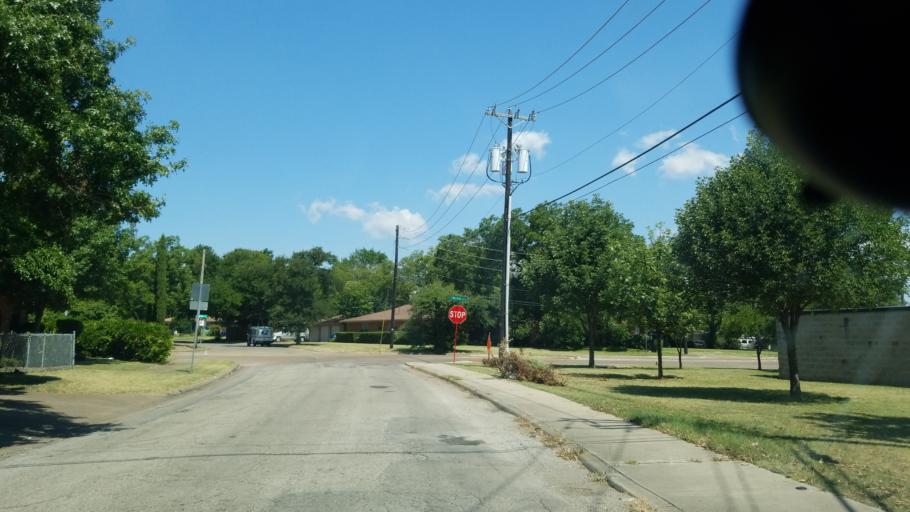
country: US
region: Texas
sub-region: Dallas County
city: Cockrell Hill
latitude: 32.7193
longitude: -96.8368
